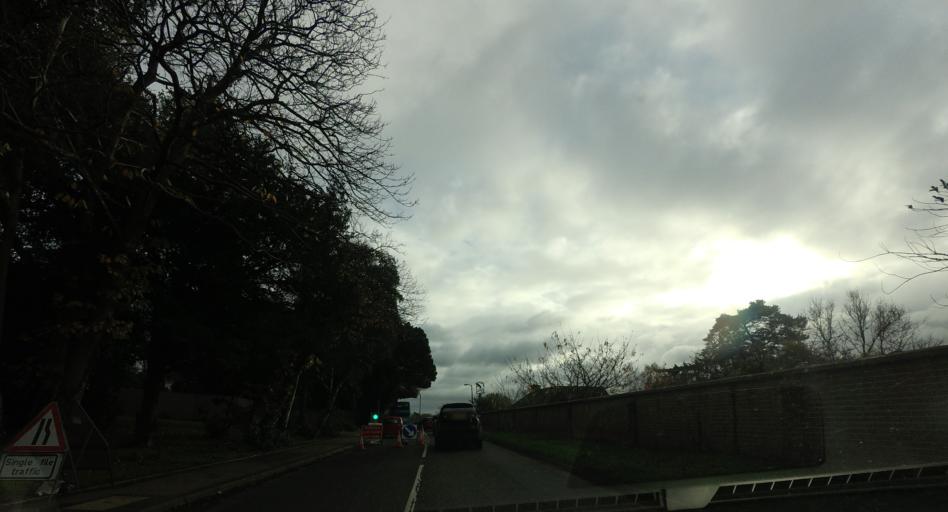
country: GB
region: England
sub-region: Kent
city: Hawkhurst
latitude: 51.0458
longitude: 0.5173
